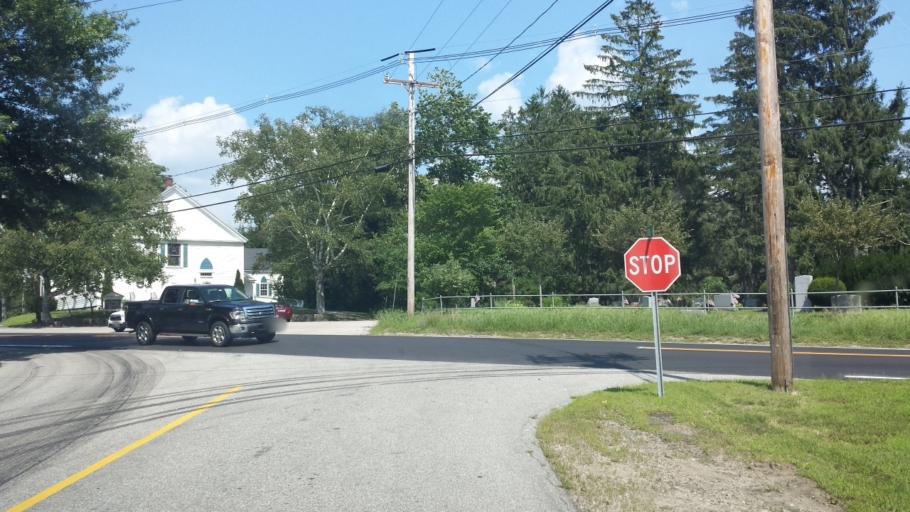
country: US
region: Maine
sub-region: York County
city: Arundel
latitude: 43.3813
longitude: -70.4775
